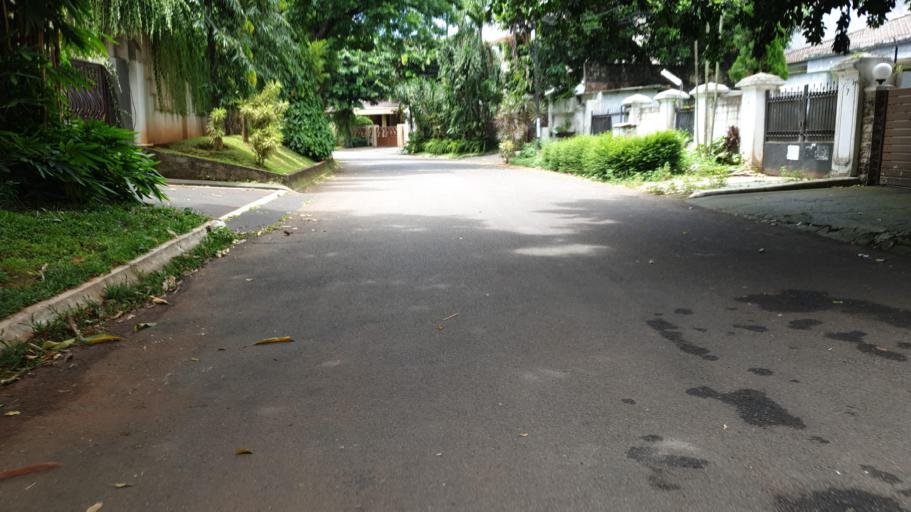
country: ID
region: Banten
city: South Tangerang
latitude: -6.2779
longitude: 106.7871
